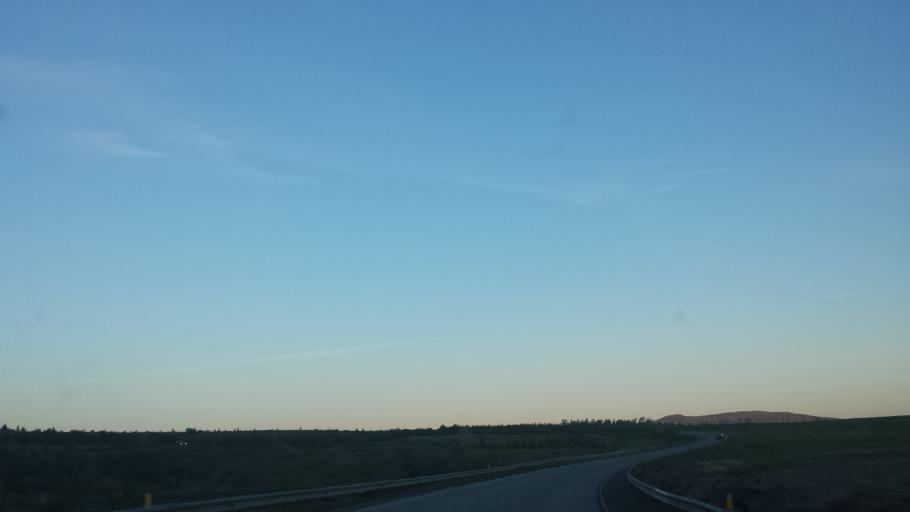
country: IS
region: Capital Region
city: Mosfellsbaer
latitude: 64.2046
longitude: -21.7080
